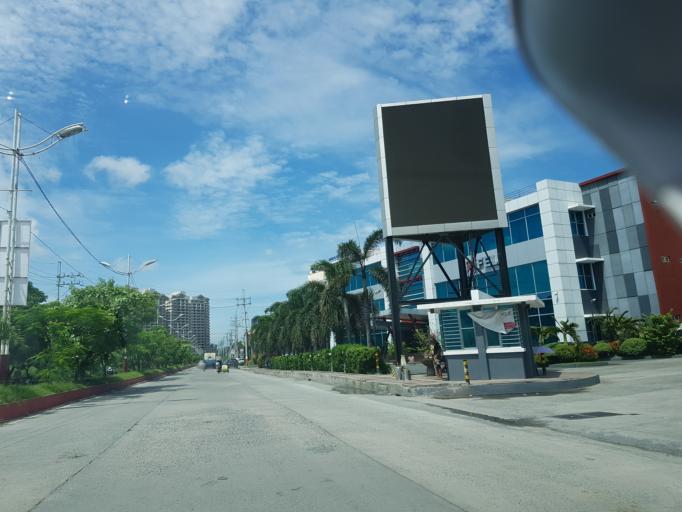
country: PH
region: Calabarzon
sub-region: Province of Rizal
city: Pateros
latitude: 14.5315
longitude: 121.0673
